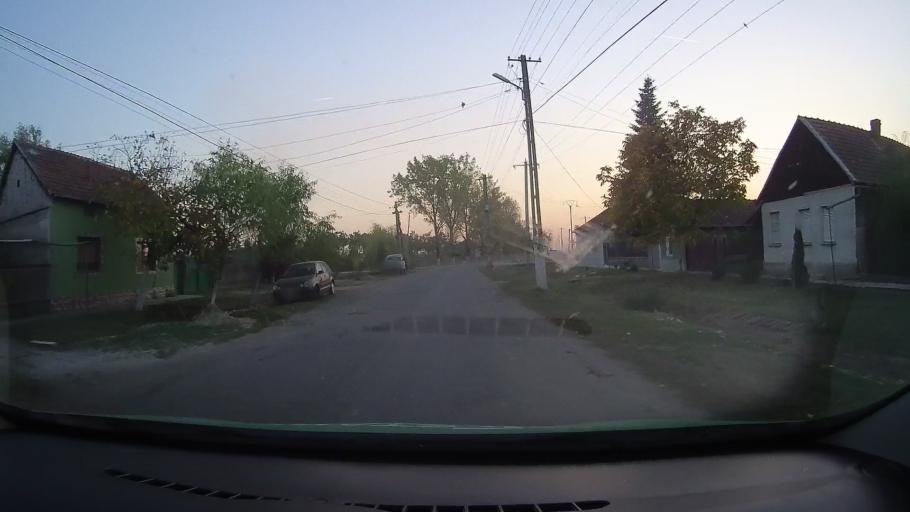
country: RO
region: Arad
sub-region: Comuna Olari
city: Olari
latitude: 46.3811
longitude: 21.5437
